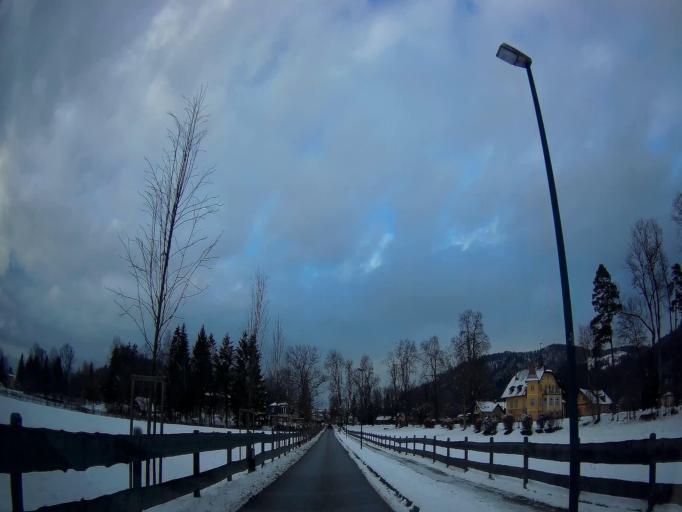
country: AT
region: Salzburg
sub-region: Salzburg Stadt
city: Salzburg
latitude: 47.7923
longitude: 13.0824
